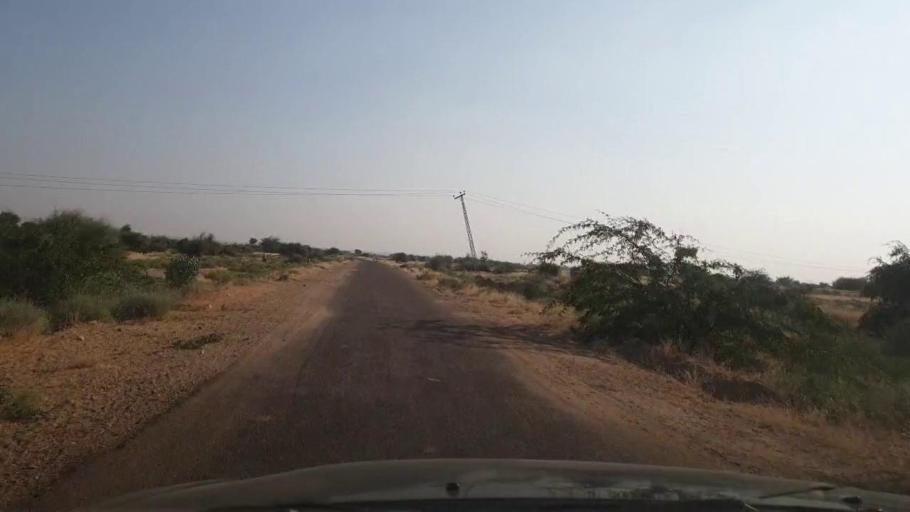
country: PK
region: Sindh
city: Jamshoro
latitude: 25.3464
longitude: 67.8382
